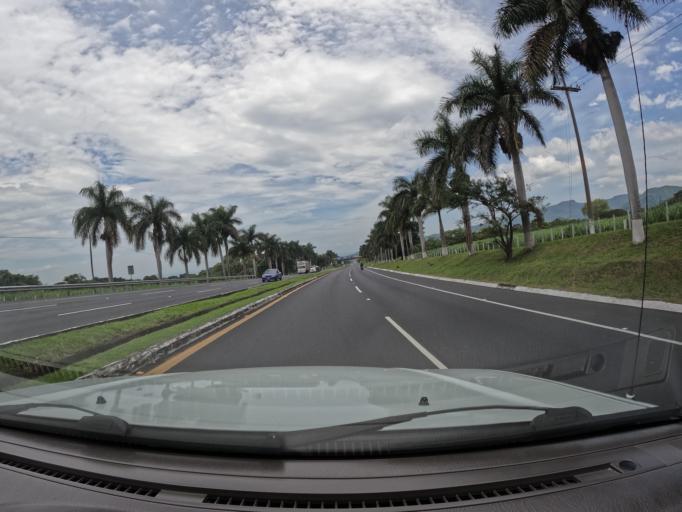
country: GT
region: Escuintla
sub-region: Municipio de Escuintla
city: Escuintla
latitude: 14.3520
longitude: -90.7842
